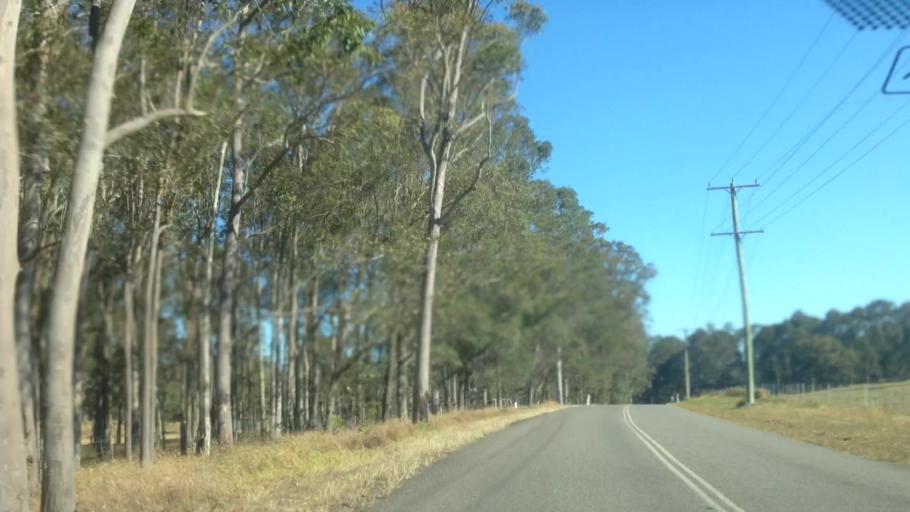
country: AU
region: New South Wales
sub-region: Lake Macquarie Shire
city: Cooranbong
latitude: -33.1138
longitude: 151.4480
